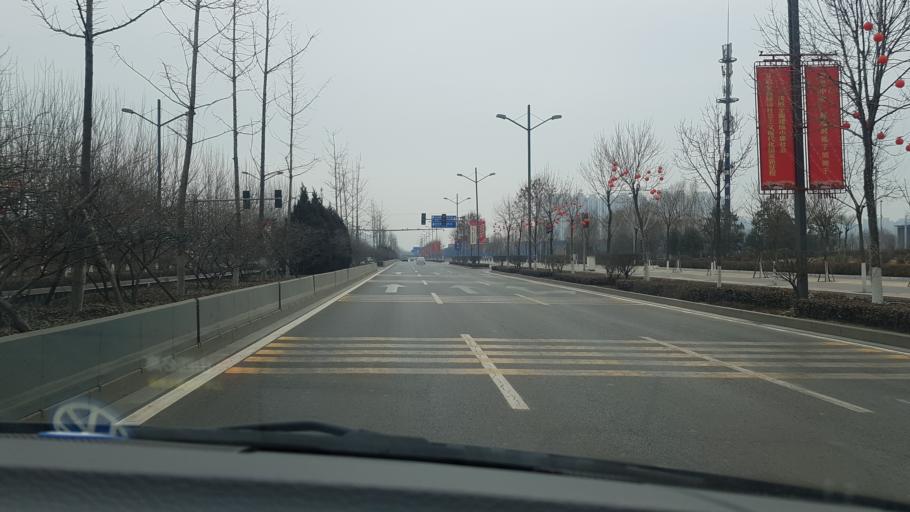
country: CN
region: Shanxi Sheng
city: Qianfeng
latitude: 37.8025
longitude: 112.5307
